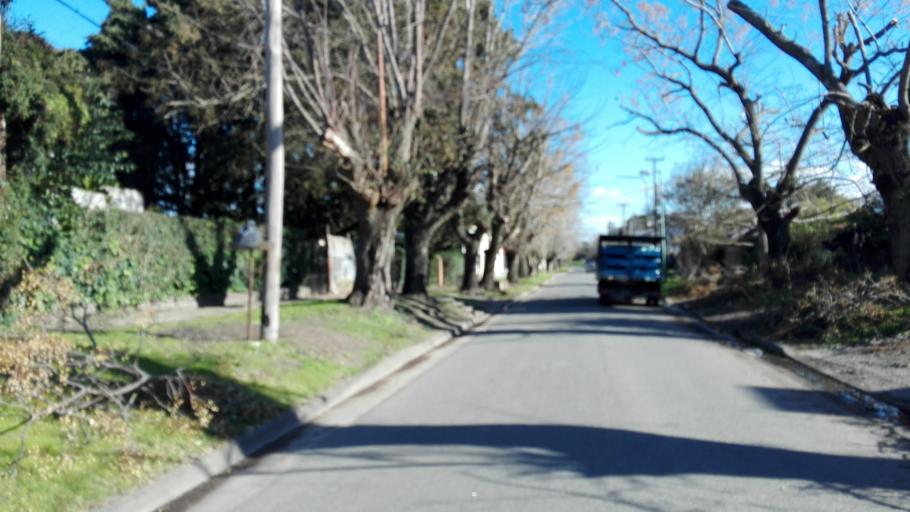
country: AR
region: Buenos Aires
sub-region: Partido de La Plata
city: La Plata
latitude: -34.8793
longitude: -58.0052
